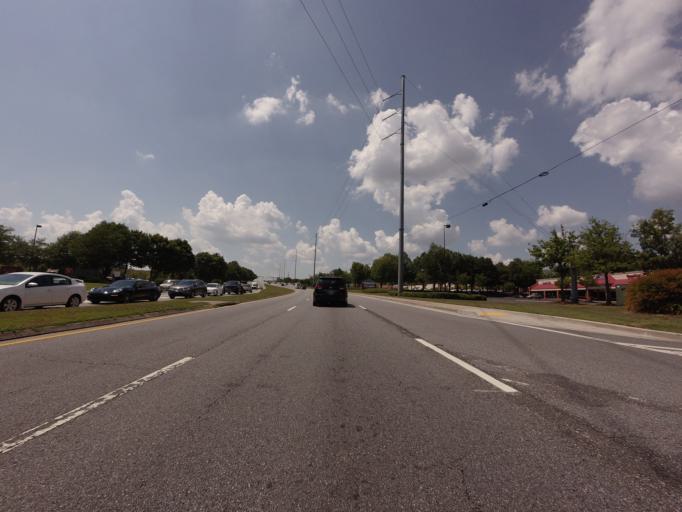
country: US
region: Georgia
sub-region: Fulton County
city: Johns Creek
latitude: 34.0146
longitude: -84.1854
